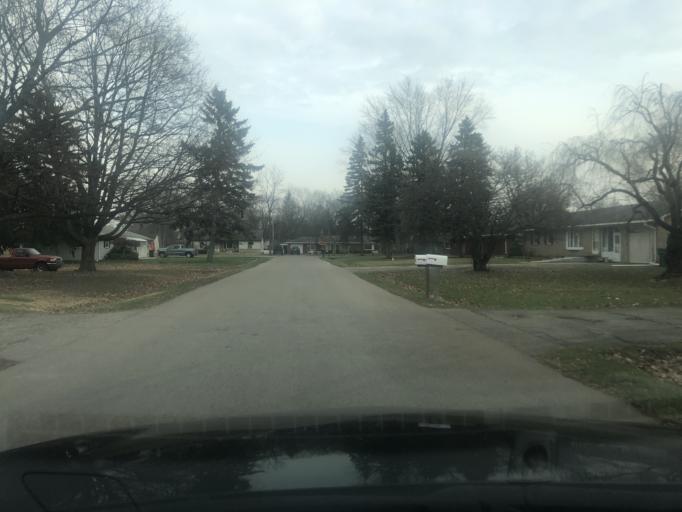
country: US
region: Michigan
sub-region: Wayne County
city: Belleville
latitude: 42.2177
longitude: -83.4825
